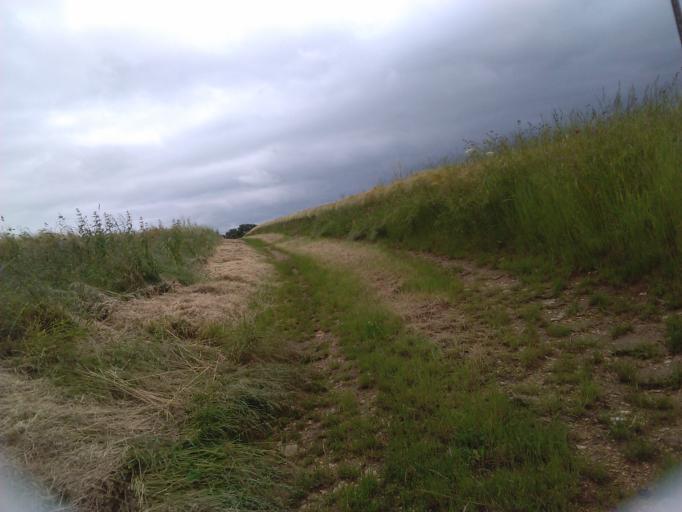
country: FR
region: Centre
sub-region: Departement du Cher
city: Sancerre
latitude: 47.3132
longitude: 2.7236
